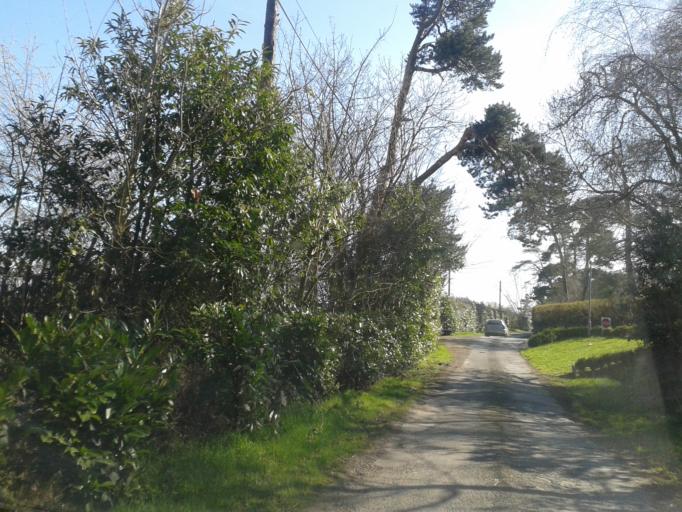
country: IE
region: Leinster
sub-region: Wicklow
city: Arklow
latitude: 52.8438
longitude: -6.1201
